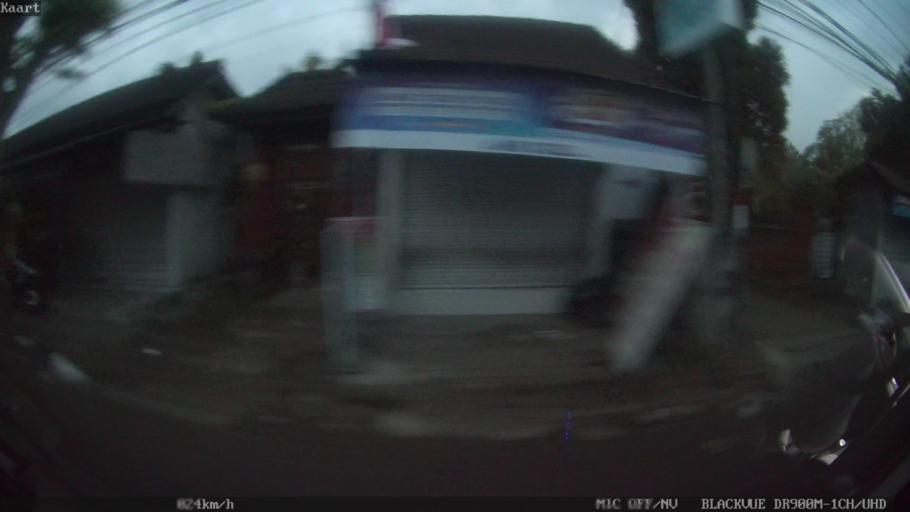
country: ID
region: Bali
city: Banjar Parekan
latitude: -8.5670
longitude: 115.2202
